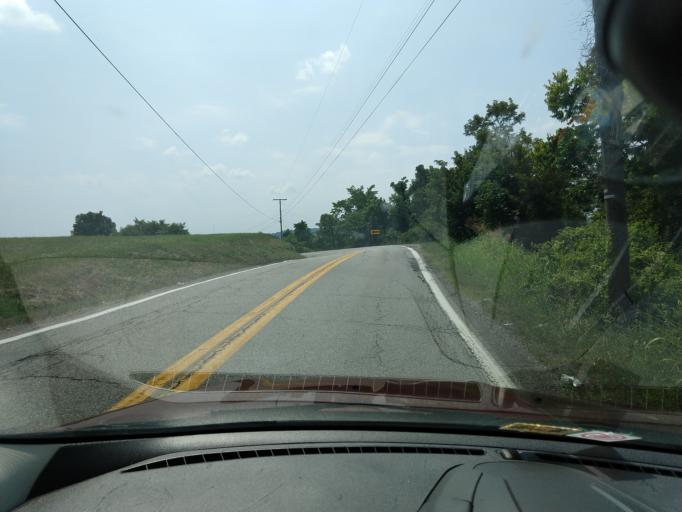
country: US
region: West Virginia
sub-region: Mason County
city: New Haven
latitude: 38.8648
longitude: -81.8911
